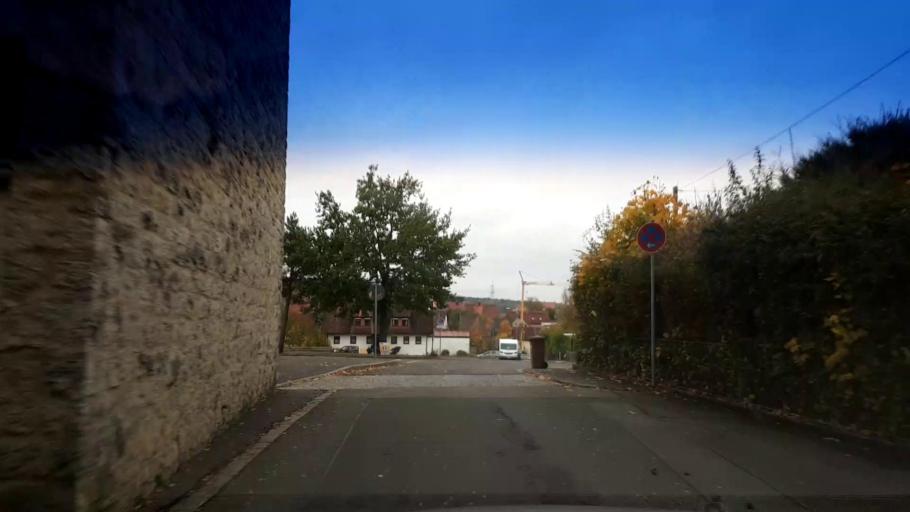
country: DE
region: Bavaria
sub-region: Upper Franconia
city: Schesslitz
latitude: 49.9761
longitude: 11.0381
